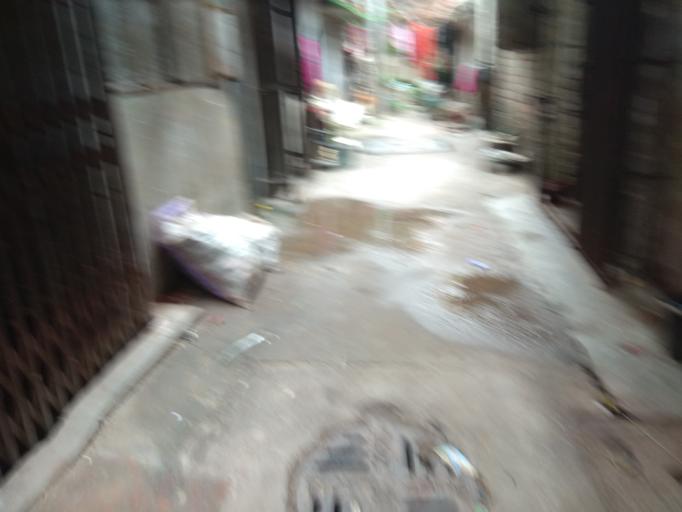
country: BD
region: Dhaka
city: Azimpur
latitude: 23.8054
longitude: 90.3553
